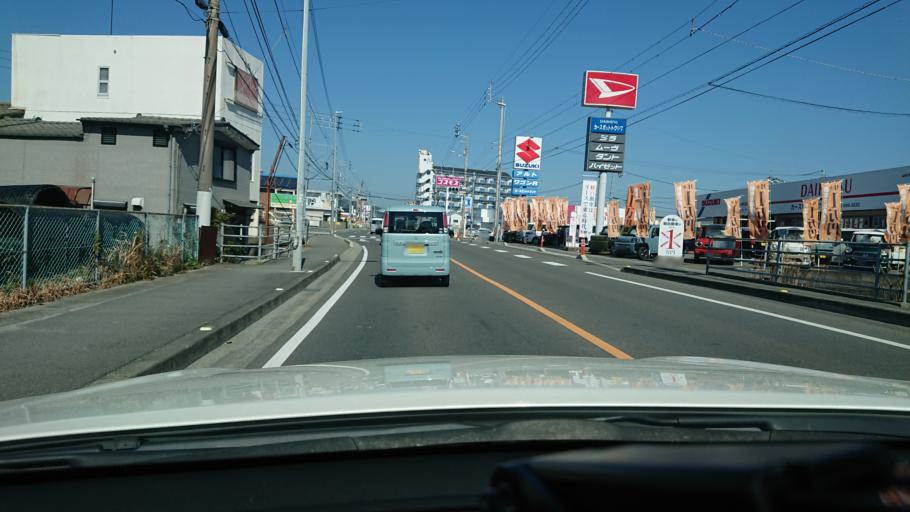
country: JP
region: Tokushima
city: Narutocho-mitsuishi
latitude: 34.1438
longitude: 134.5936
